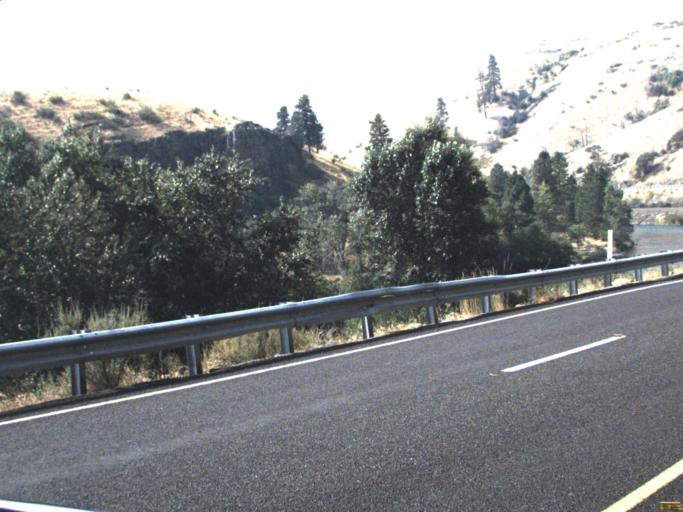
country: US
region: Washington
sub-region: Kittitas County
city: Ellensburg
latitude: 47.1221
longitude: -120.7249
